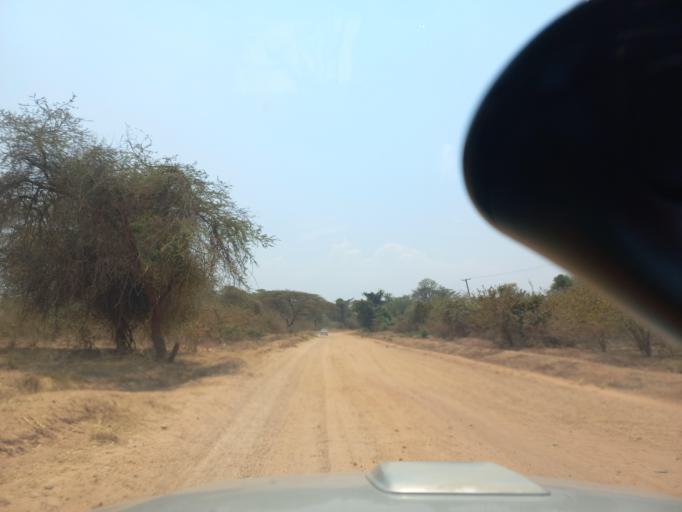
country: ZW
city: Chirundu
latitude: -15.9344
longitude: 28.8716
